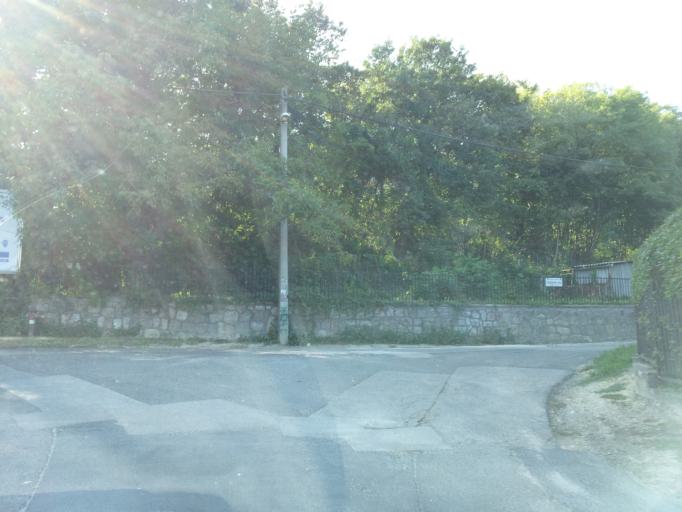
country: HU
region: Budapest
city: Budapest XII. keruelet
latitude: 47.5290
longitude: 18.9839
